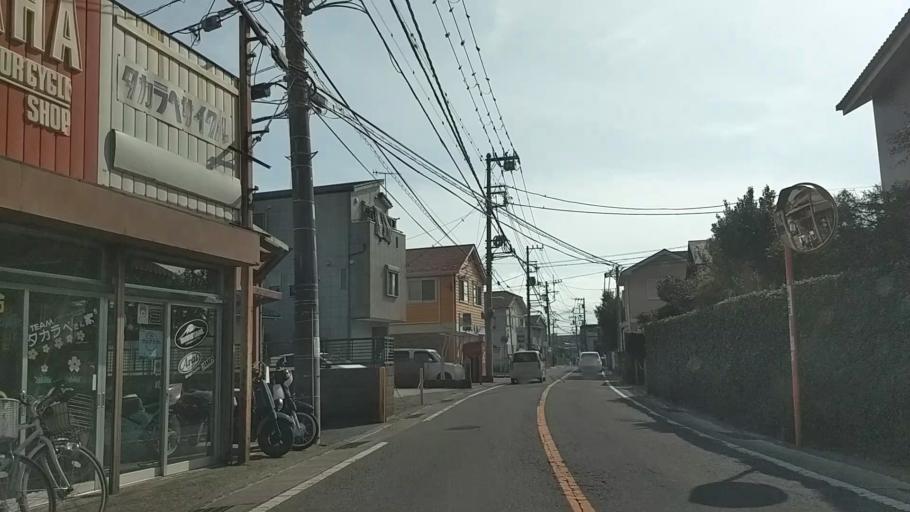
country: JP
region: Kanagawa
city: Chigasaki
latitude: 35.3409
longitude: 139.3827
